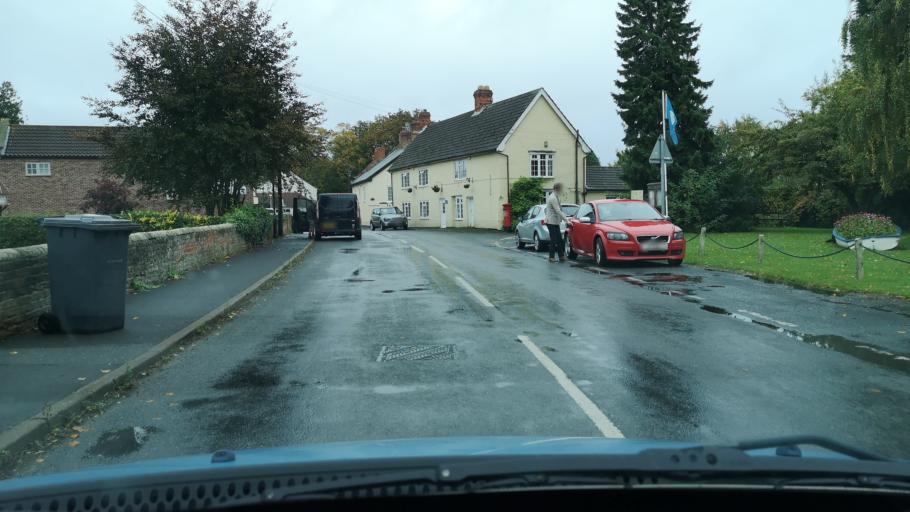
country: GB
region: England
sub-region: Doncaster
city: Stainforth
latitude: 53.6107
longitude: -1.0120
